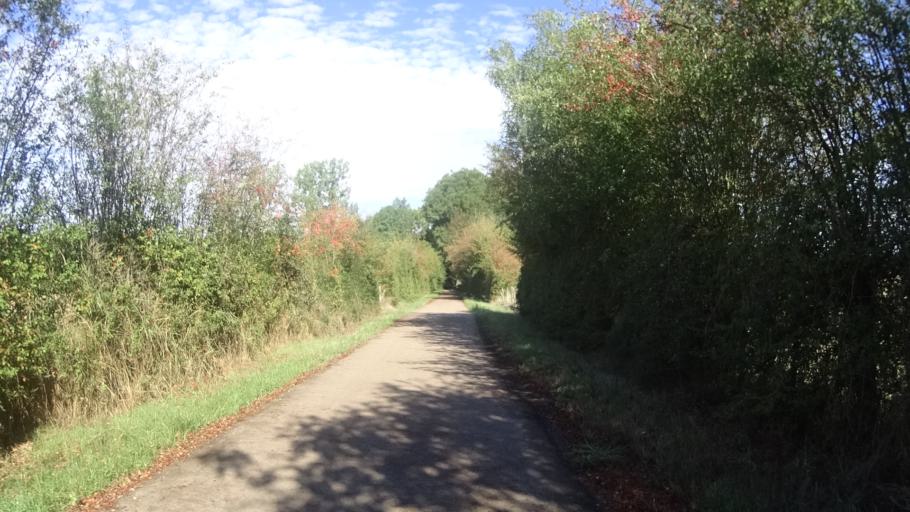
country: FR
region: Centre
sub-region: Departement du Cher
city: Saint-Satur
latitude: 47.3263
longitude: 2.8644
